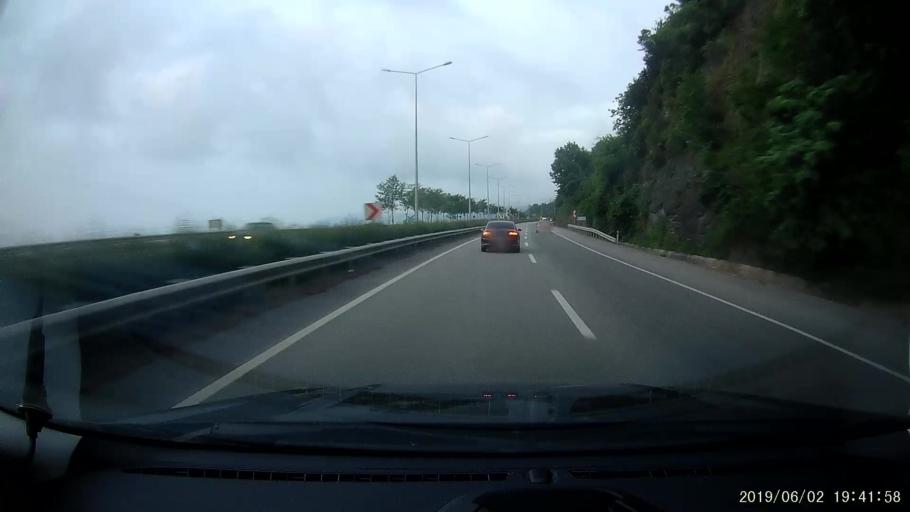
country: TR
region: Giresun
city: Kesap
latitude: 40.9156
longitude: 38.4924
